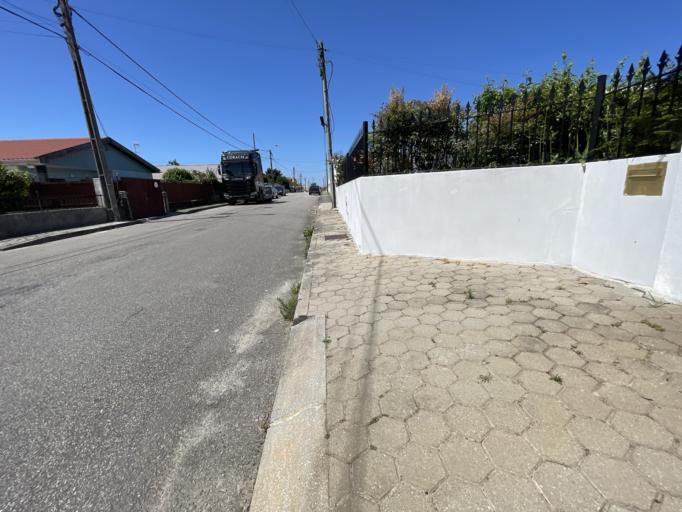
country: PT
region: Aveiro
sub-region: Ovar
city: Cortegaca
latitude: 40.9449
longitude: -8.6264
